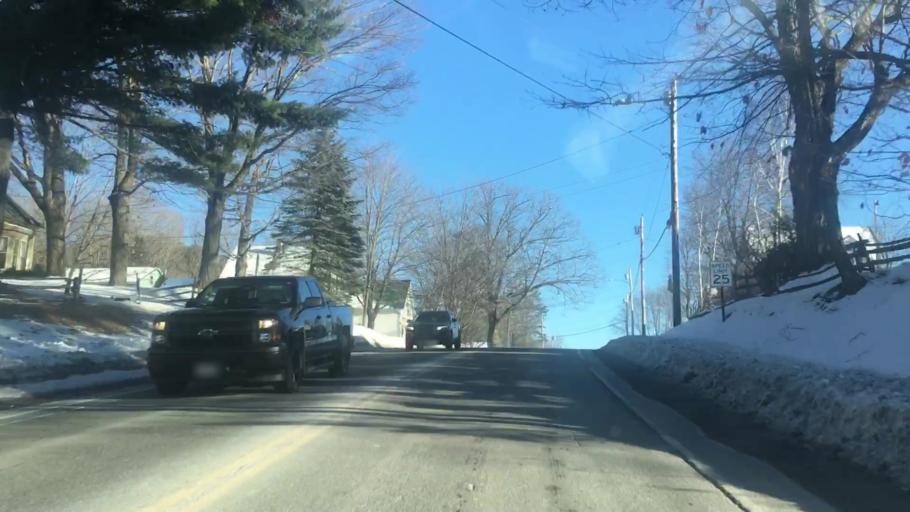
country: US
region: Maine
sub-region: Somerset County
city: Norridgewock
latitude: 44.7127
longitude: -69.7876
